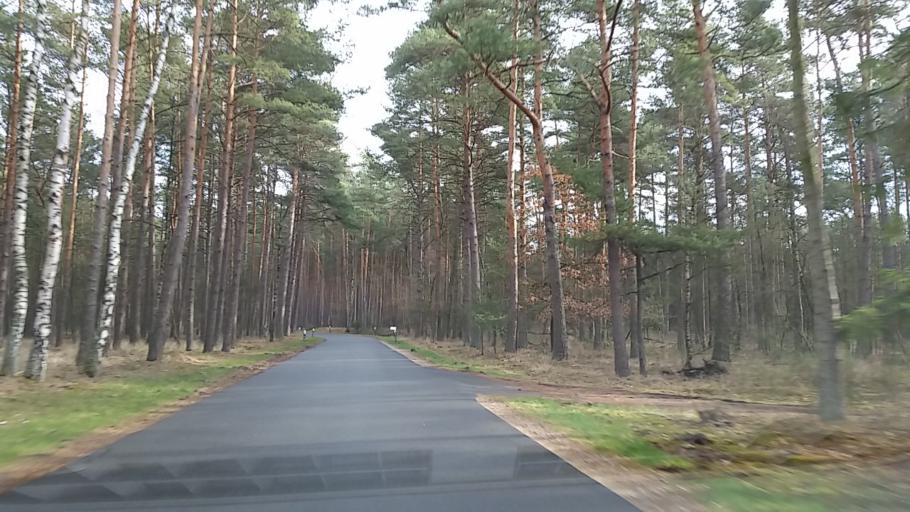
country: DE
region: Lower Saxony
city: Soltendieck
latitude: 52.8419
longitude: 10.7633
